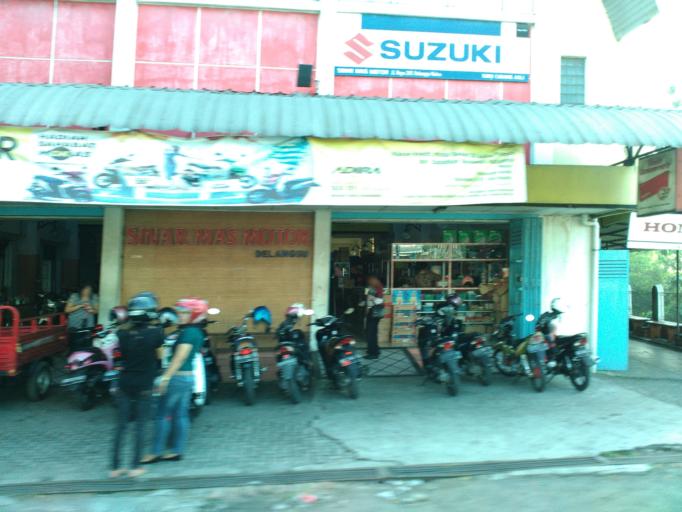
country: ID
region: Central Java
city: Delanggu
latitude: -7.6266
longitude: 110.6962
